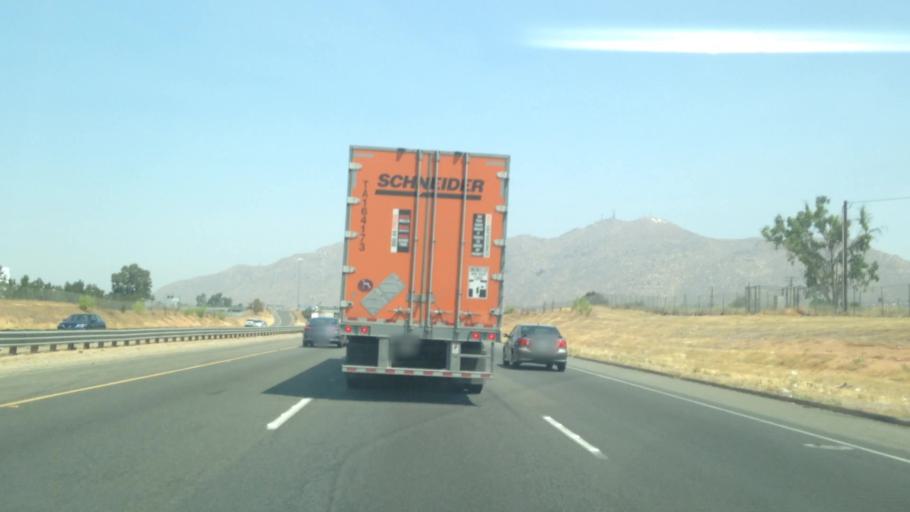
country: US
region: California
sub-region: Riverside County
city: March Air Force Base
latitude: 33.9258
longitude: -117.2886
